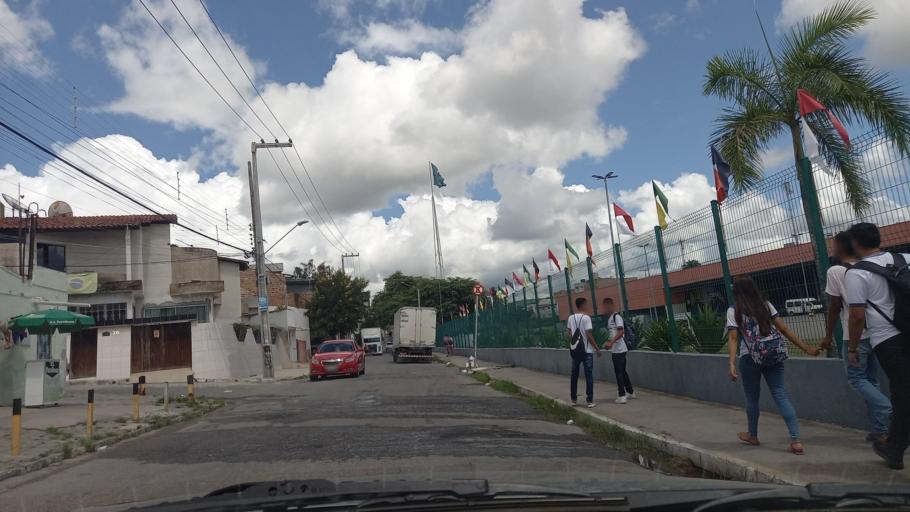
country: BR
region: Pernambuco
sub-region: Caruaru
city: Caruaru
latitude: -8.2961
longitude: -35.9706
